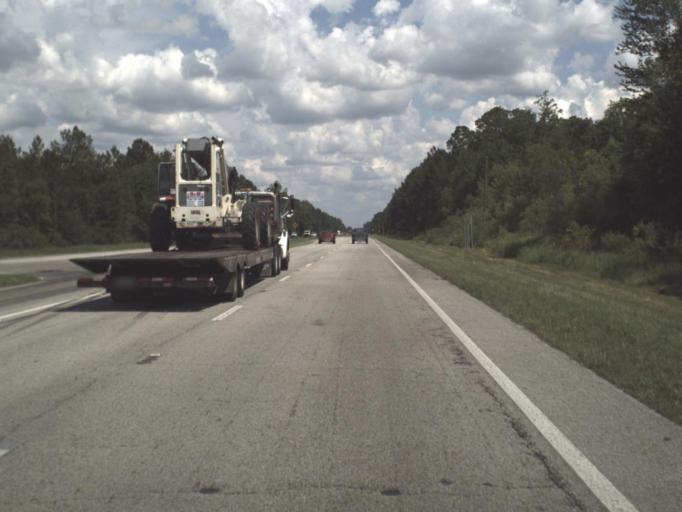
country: US
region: Florida
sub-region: Alachua County
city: Alachua
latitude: 29.7235
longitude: -82.3676
